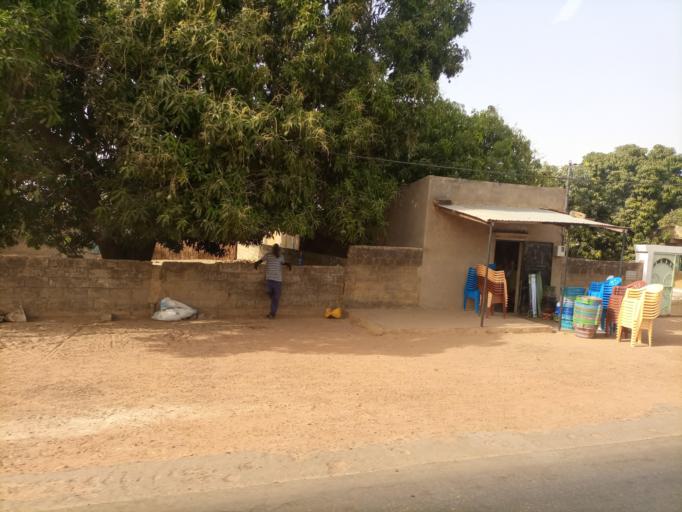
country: SN
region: Fatick
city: Foundiougne
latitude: 14.1218
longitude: -16.4317
